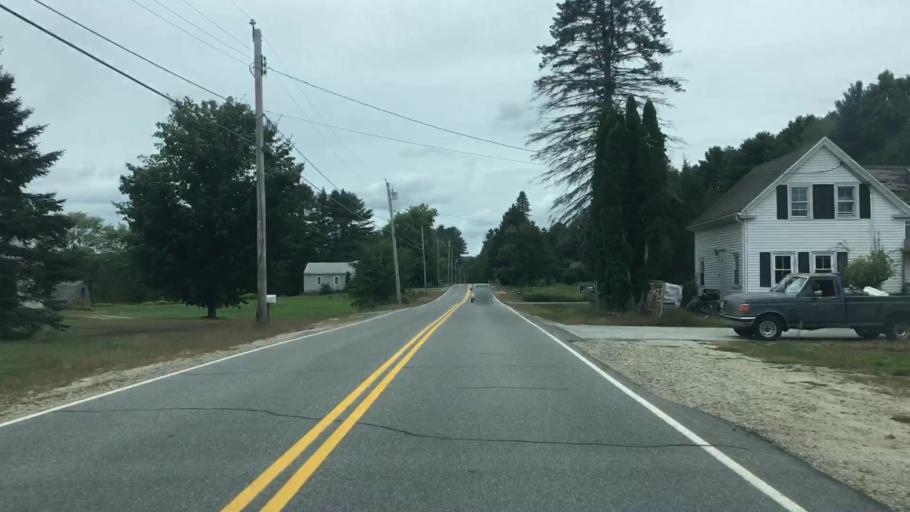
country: US
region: Maine
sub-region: Cumberland County
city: Yarmouth
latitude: 43.8665
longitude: -70.2265
